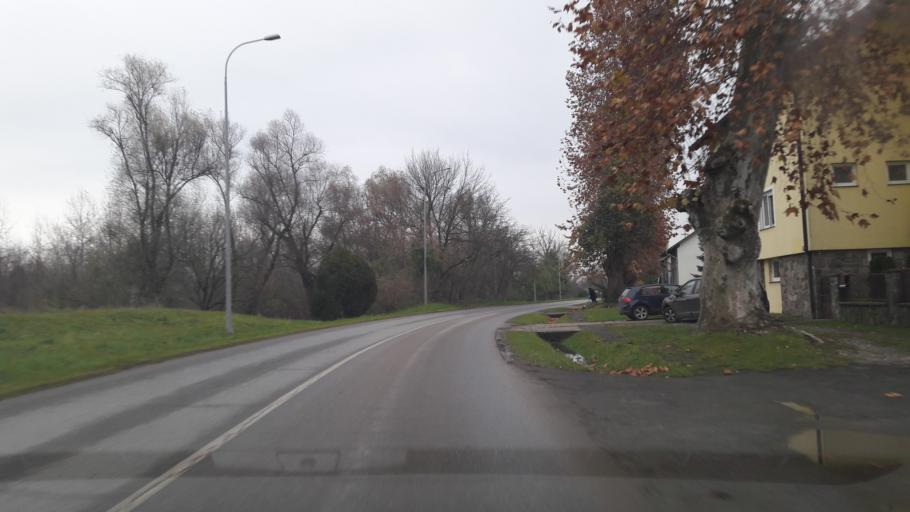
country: HR
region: Osjecko-Baranjska
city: Visnjevac
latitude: 45.5737
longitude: 18.6009
